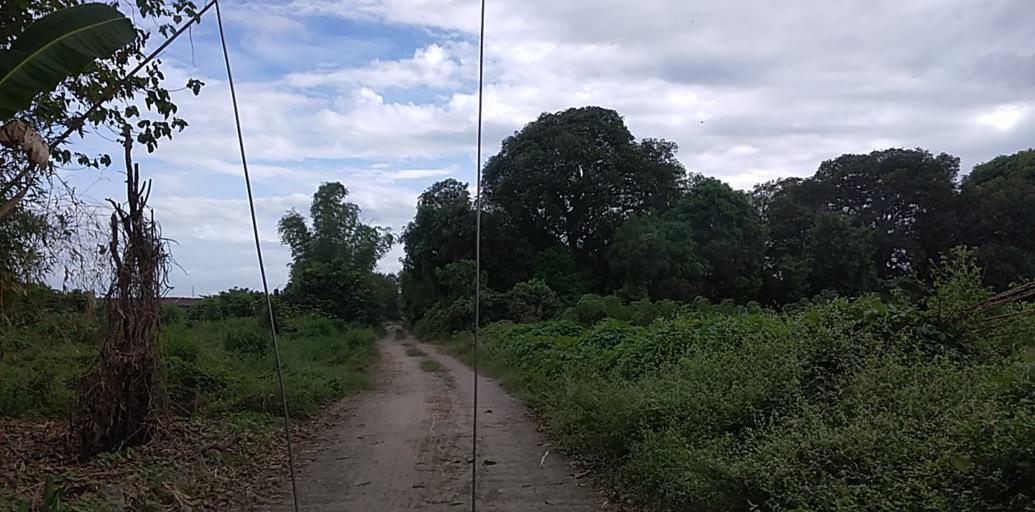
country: PH
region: Central Luzon
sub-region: Province of Pampanga
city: Pulung Santol
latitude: 15.0363
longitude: 120.5608
